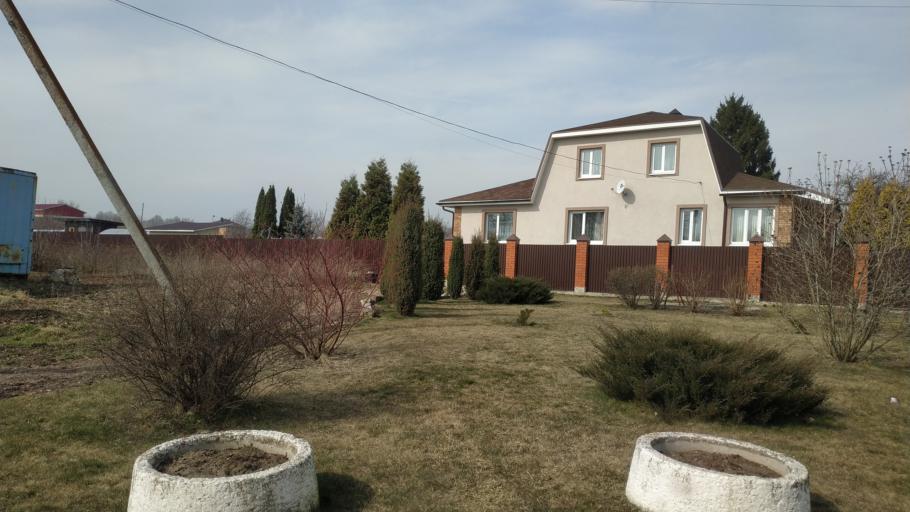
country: RU
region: Moskovskaya
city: Voskresensk
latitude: 55.3391
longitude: 38.6221
